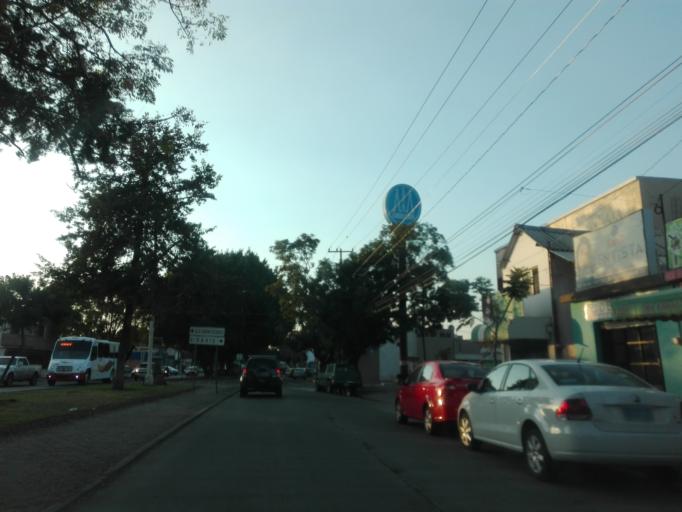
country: MX
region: Guanajuato
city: Leon
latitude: 21.1064
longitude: -101.6689
